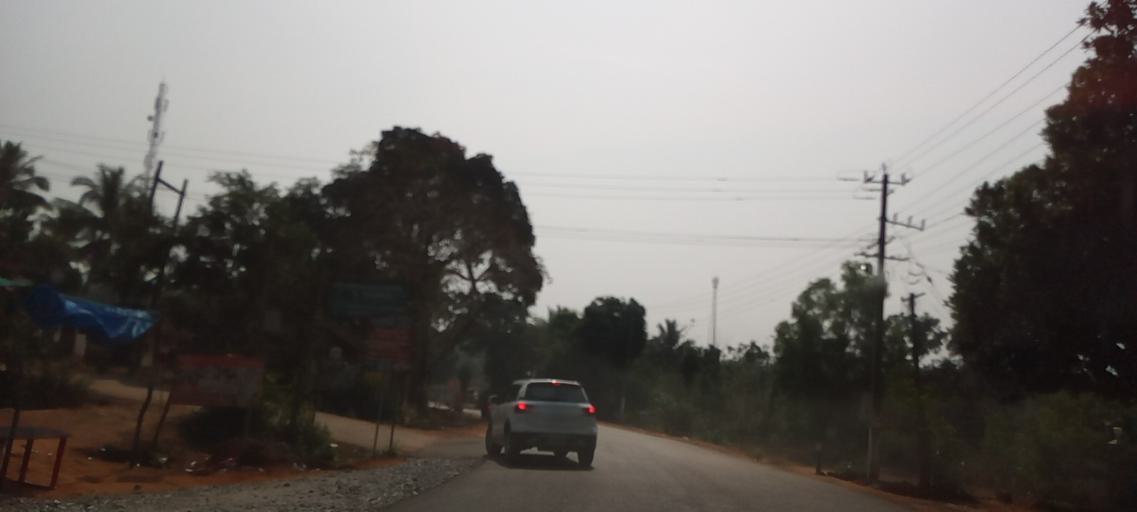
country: IN
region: Karnataka
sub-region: Udupi
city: Someshwar
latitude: 13.5277
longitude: 74.9231
